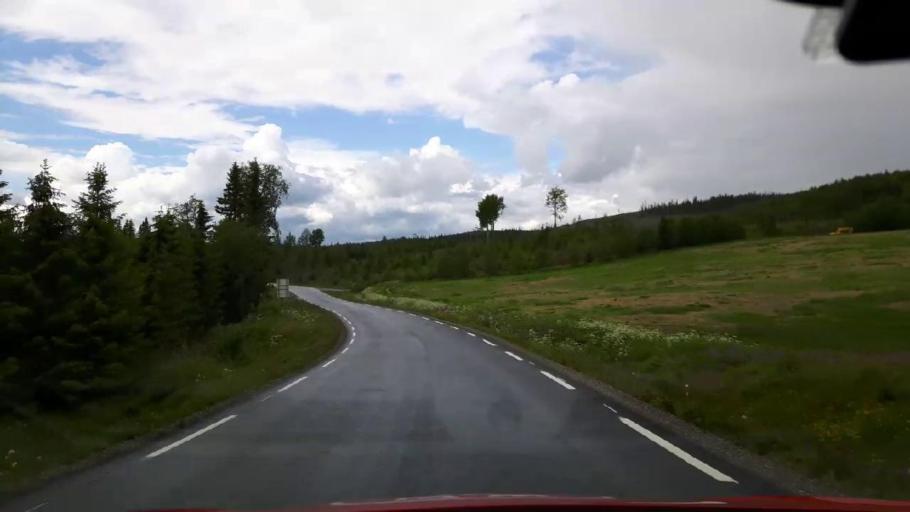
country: NO
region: Nord-Trondelag
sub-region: Lierne
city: Sandvika
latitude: 64.0976
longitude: 14.0341
